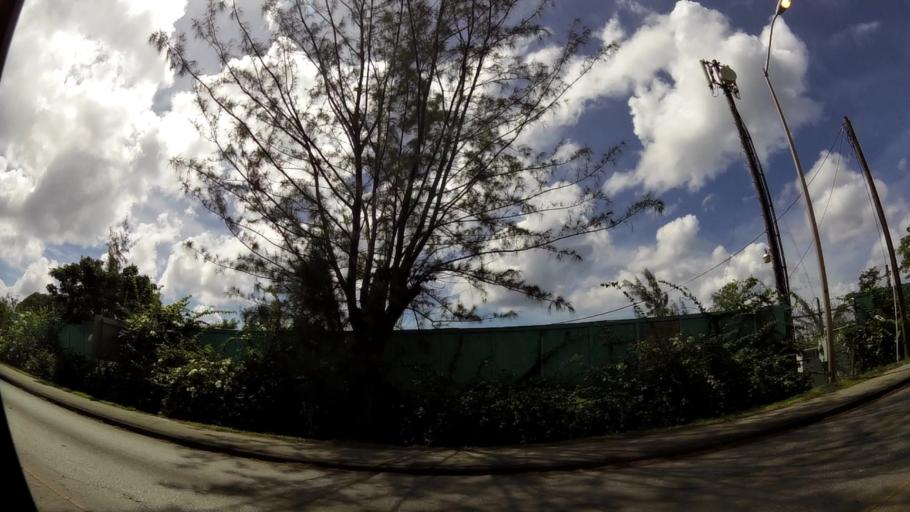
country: BB
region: Saint Michael
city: Bridgetown
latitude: 13.1309
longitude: -59.6334
